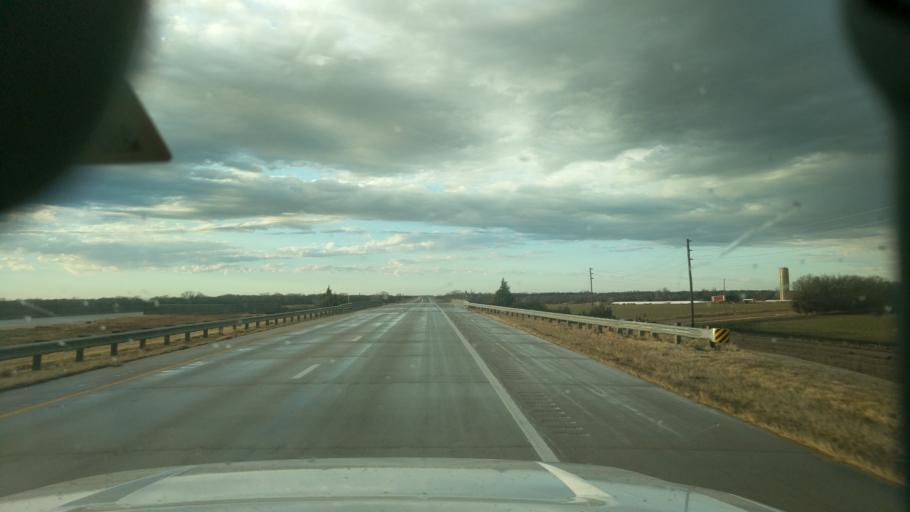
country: US
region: Kansas
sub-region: Harvey County
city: North Newton
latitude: 38.1013
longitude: -97.3710
